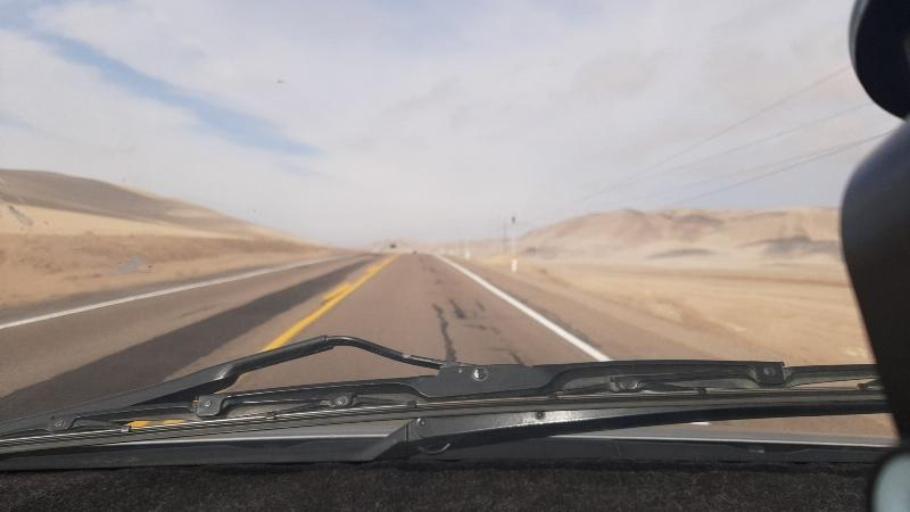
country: PE
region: Moquegua
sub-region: Provincia de Ilo
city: El Algarrobal
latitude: -17.6831
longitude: -71.2352
